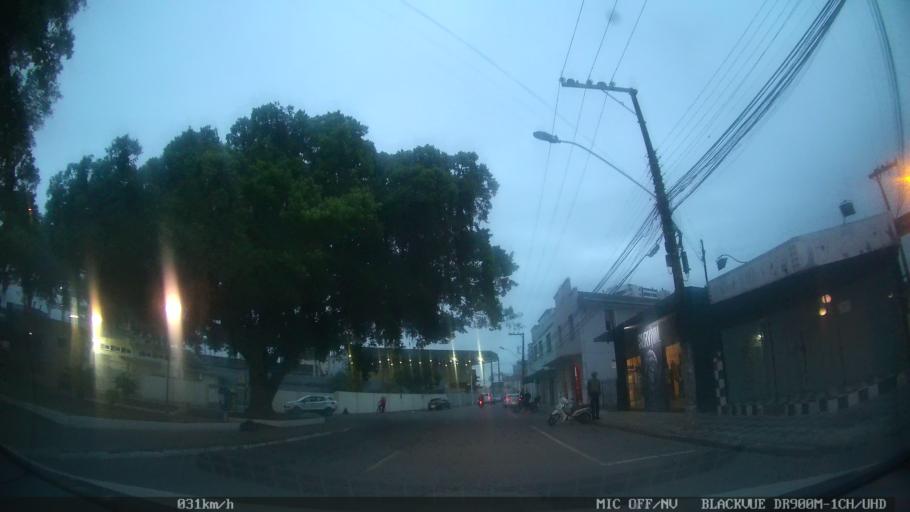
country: BR
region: Santa Catarina
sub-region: Itajai
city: Itajai
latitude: -26.9020
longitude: -48.6672
